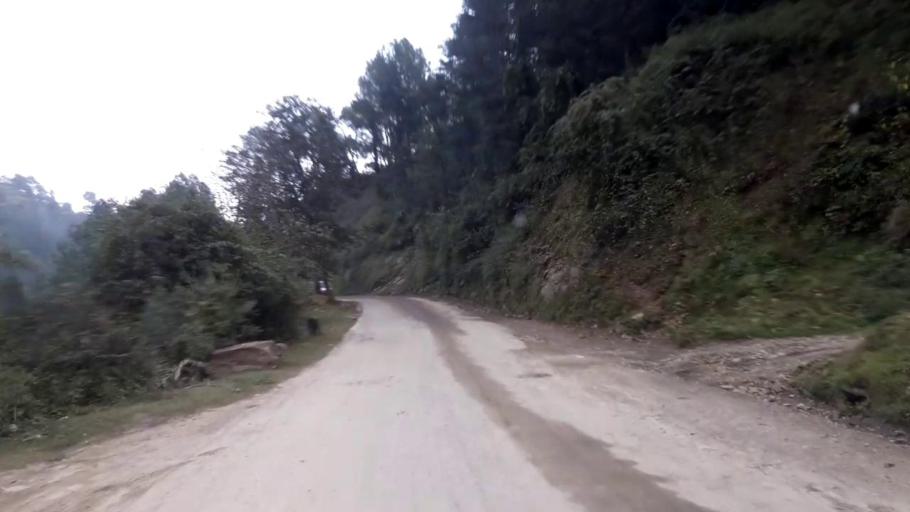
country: IN
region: Himachal Pradesh
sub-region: Shimla
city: Shimla
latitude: 31.0665
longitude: 77.1463
